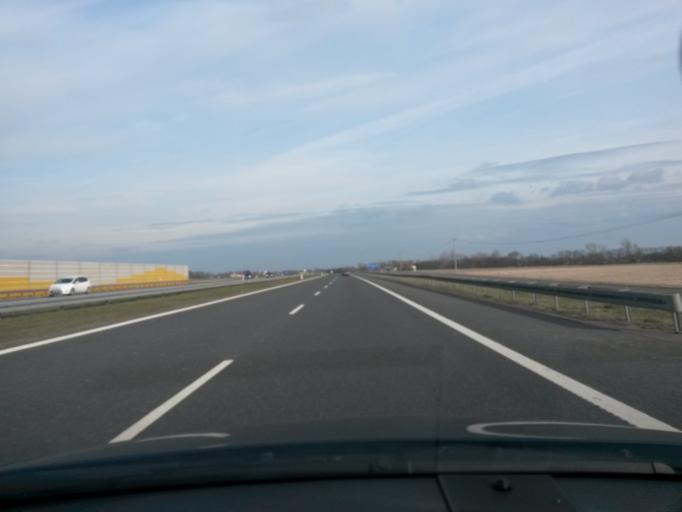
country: PL
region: Lodz Voivodeship
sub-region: Powiat poddebicki
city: Wartkowice
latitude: 52.0043
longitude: 18.9879
